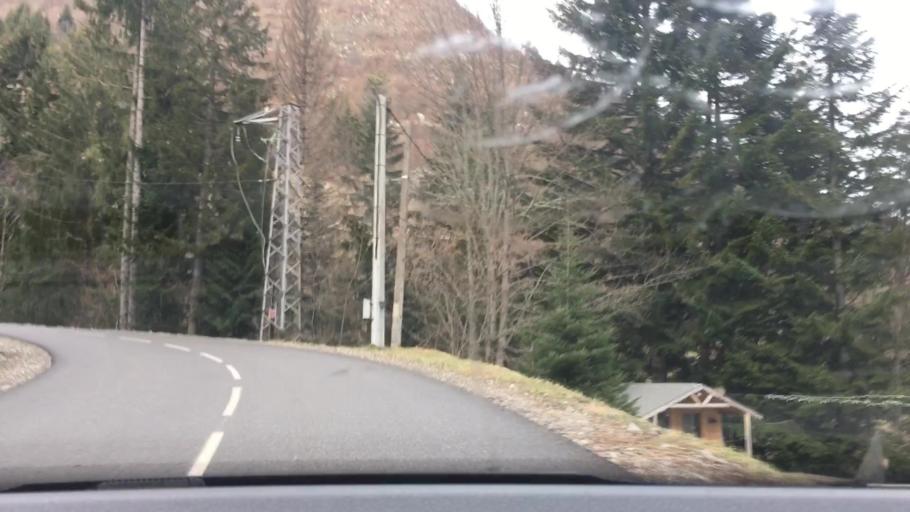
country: FR
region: Rhone-Alpes
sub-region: Departement de la Haute-Savoie
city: Abondance
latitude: 46.2861
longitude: 6.6612
